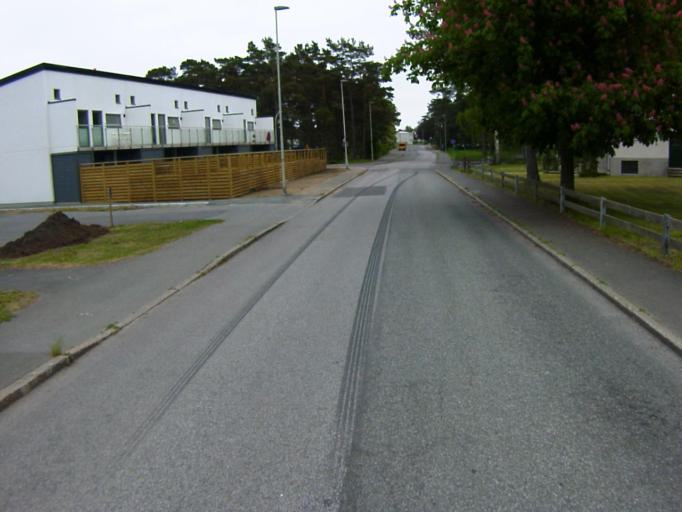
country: SE
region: Skane
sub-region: Kristianstads Kommun
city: Ahus
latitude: 55.9327
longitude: 14.3010
